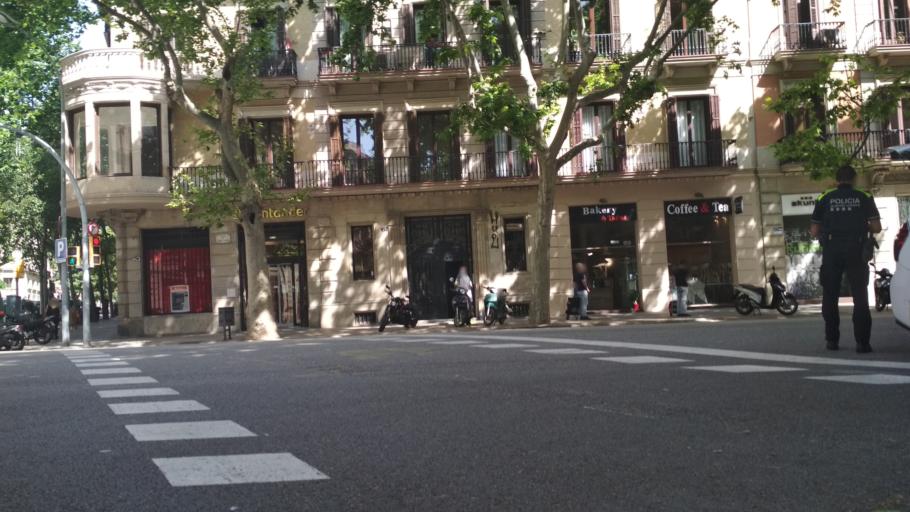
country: ES
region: Catalonia
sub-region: Provincia de Barcelona
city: Ciutat Vella
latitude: 41.3899
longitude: 2.1755
